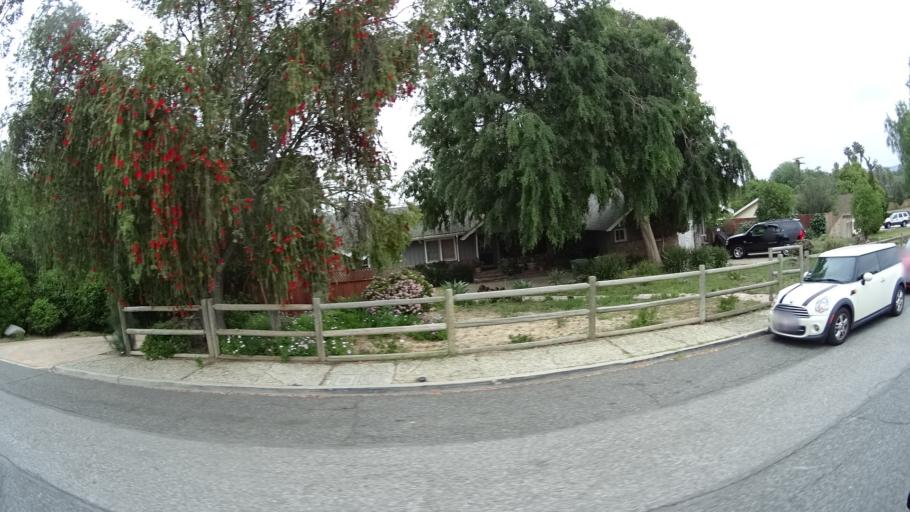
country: US
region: California
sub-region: Ventura County
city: Thousand Oaks
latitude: 34.2012
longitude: -118.8644
